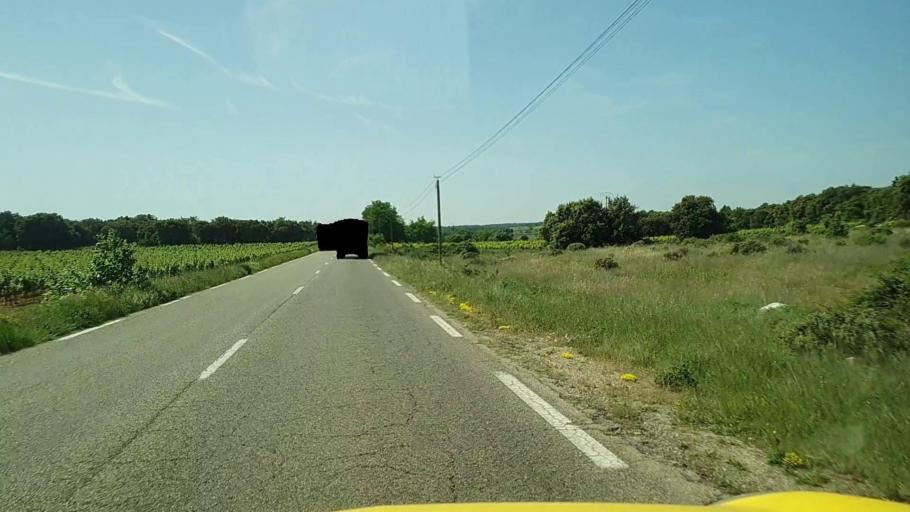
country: FR
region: Languedoc-Roussillon
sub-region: Departement du Gard
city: Connaux
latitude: 44.0505
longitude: 4.5729
